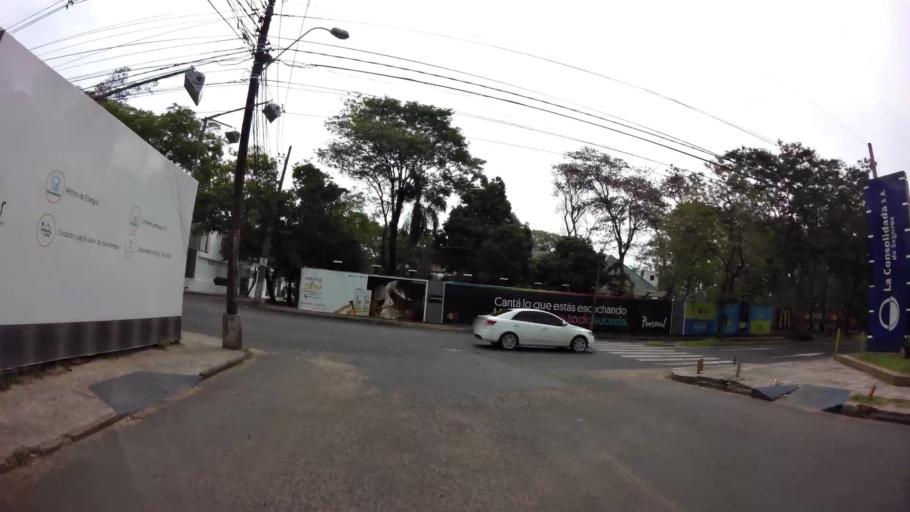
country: PY
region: Asuncion
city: Asuncion
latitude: -25.2882
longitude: -57.5891
